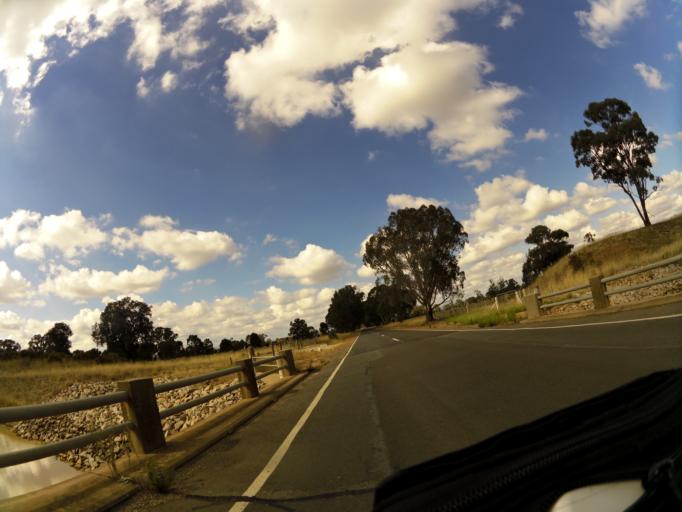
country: AU
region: Victoria
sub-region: Benalla
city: Benalla
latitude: -36.5977
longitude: 146.0108
